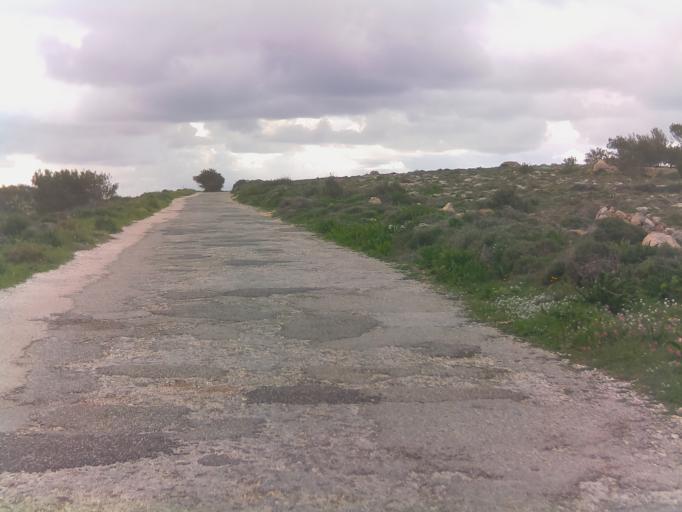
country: MT
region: Il-Mellieha
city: Mellieha
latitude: 35.9738
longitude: 14.3396
